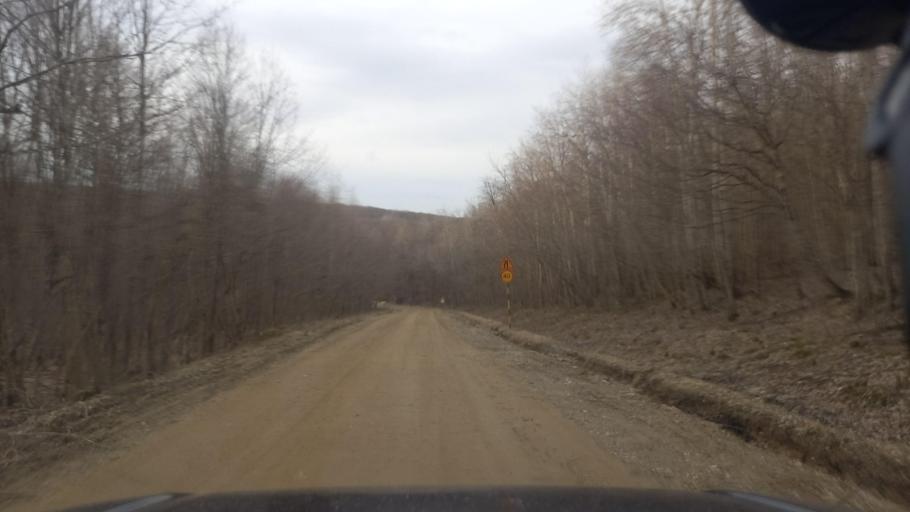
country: RU
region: Krasnodarskiy
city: Goryachiy Klyuch
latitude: 44.7033
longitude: 39.0163
